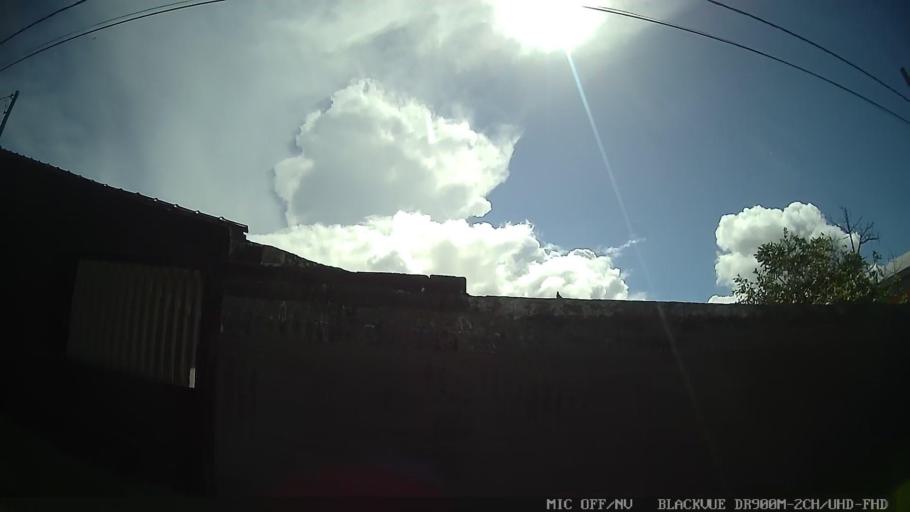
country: BR
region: Sao Paulo
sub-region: Itanhaem
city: Itanhaem
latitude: -24.2421
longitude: -46.8971
